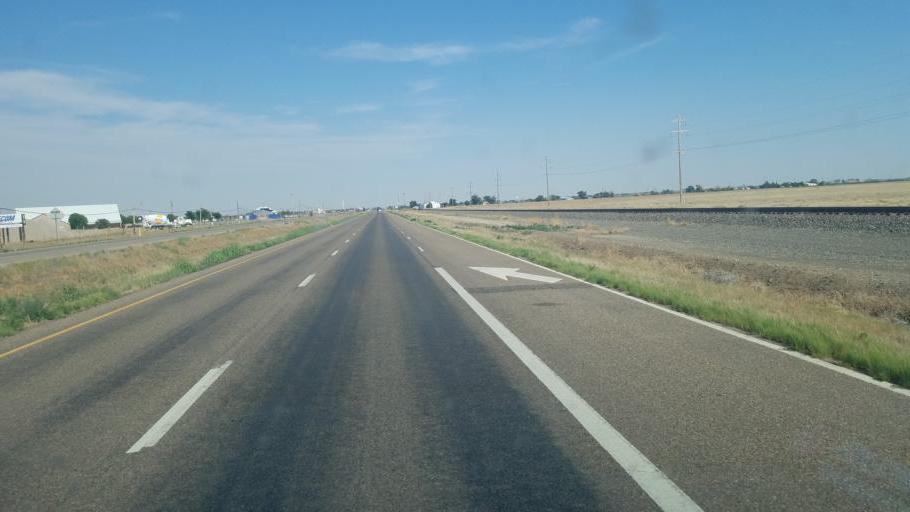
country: US
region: Colorado
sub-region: Otero County
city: Rocky Ford
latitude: 38.0305
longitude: -103.6642
